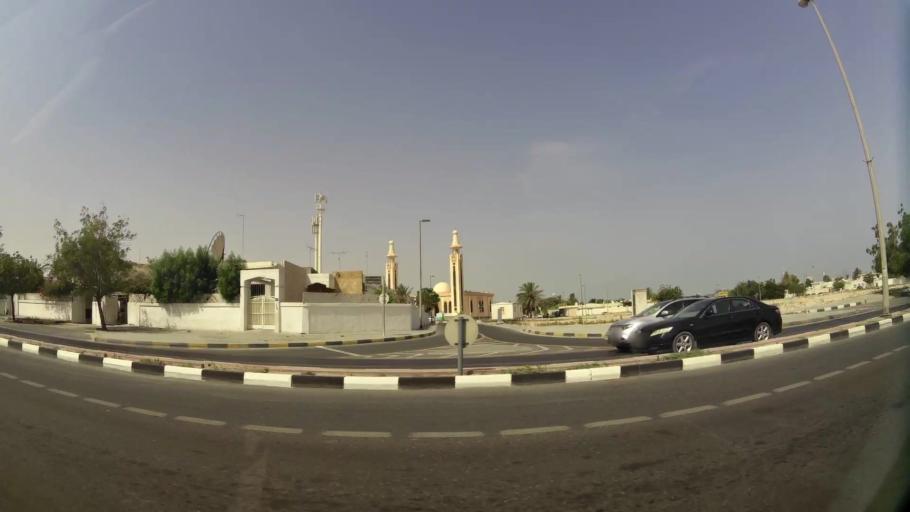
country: AE
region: Ash Shariqah
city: Sharjah
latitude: 25.3639
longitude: 55.4203
